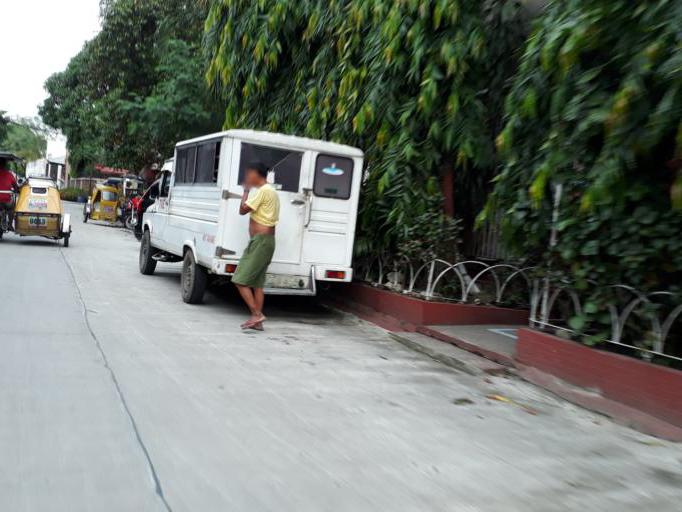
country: PH
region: Calabarzon
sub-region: Province of Rizal
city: Valenzuela
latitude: 14.6795
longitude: 120.9741
